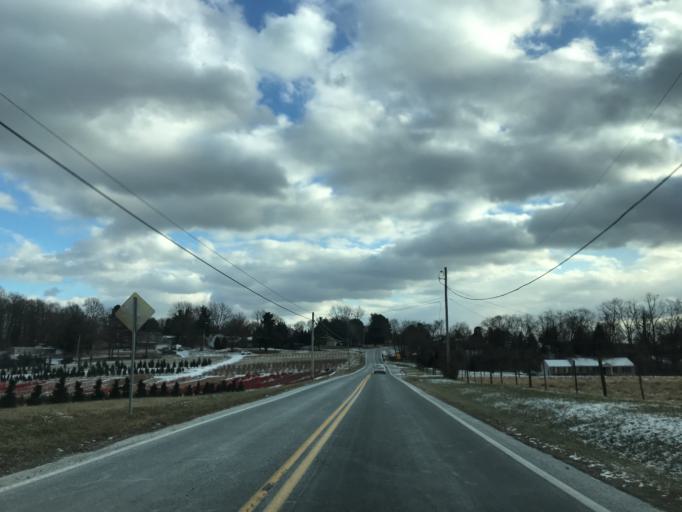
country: US
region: Maryland
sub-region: Harford County
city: Bel Air North
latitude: 39.6448
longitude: -76.3819
